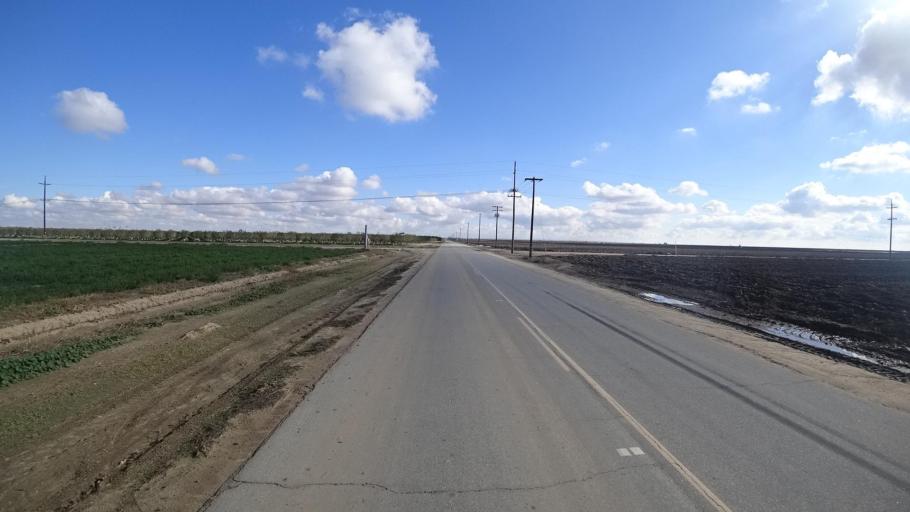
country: US
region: California
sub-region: Kern County
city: McFarland
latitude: 35.6743
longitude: -119.2772
